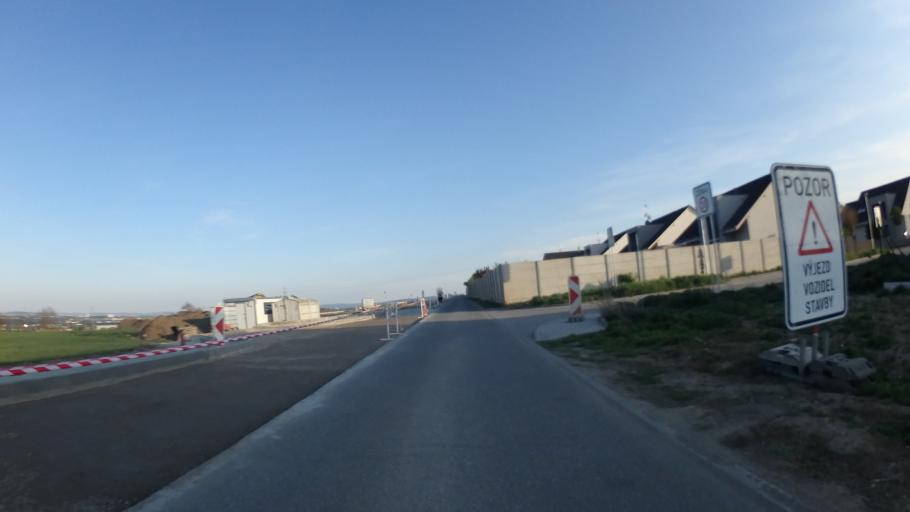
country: CZ
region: South Moravian
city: Moravany
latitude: 49.1521
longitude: 16.5829
